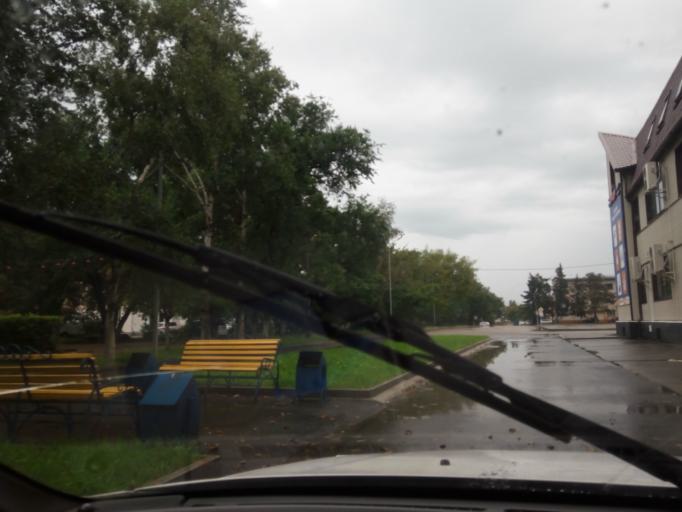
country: RU
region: Primorskiy
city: Dal'nerechensk
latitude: 45.9321
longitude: 133.7266
